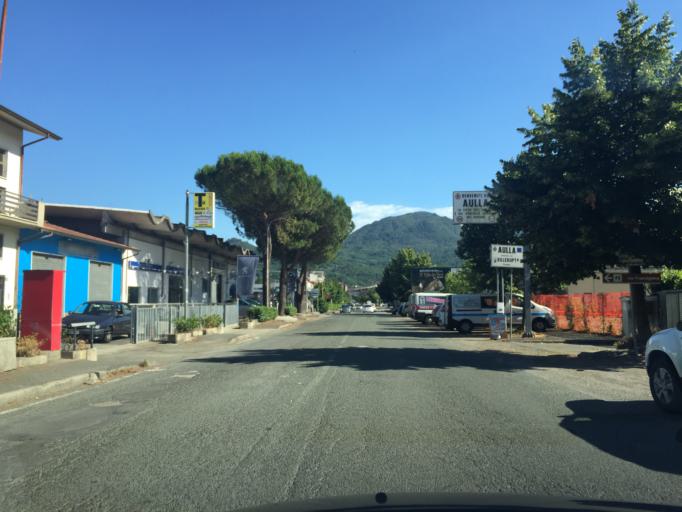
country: IT
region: Tuscany
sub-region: Provincia di Massa-Carrara
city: Terrarossa
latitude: 44.2184
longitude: 9.9660
